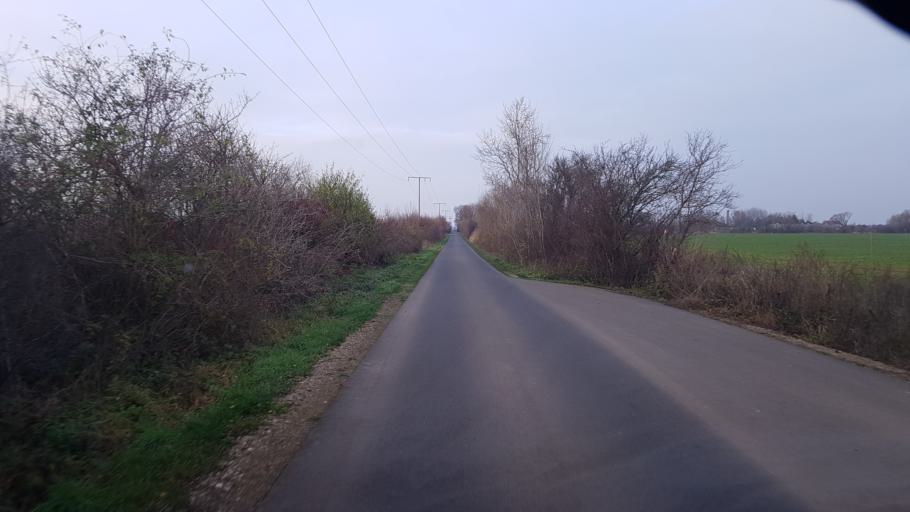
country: DE
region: Brandenburg
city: Ziltendorf
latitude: 52.2184
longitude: 14.6336
